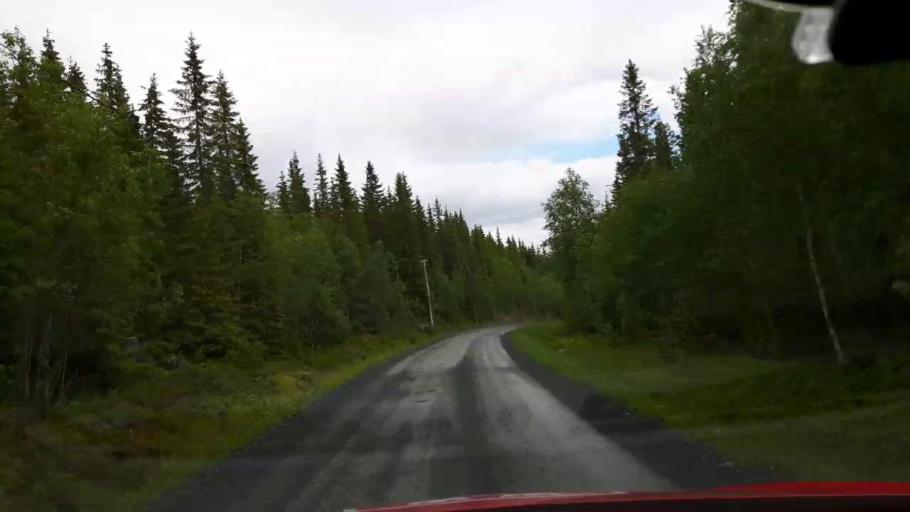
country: NO
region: Nord-Trondelag
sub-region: Lierne
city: Sandvika
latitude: 64.1597
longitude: 14.0393
